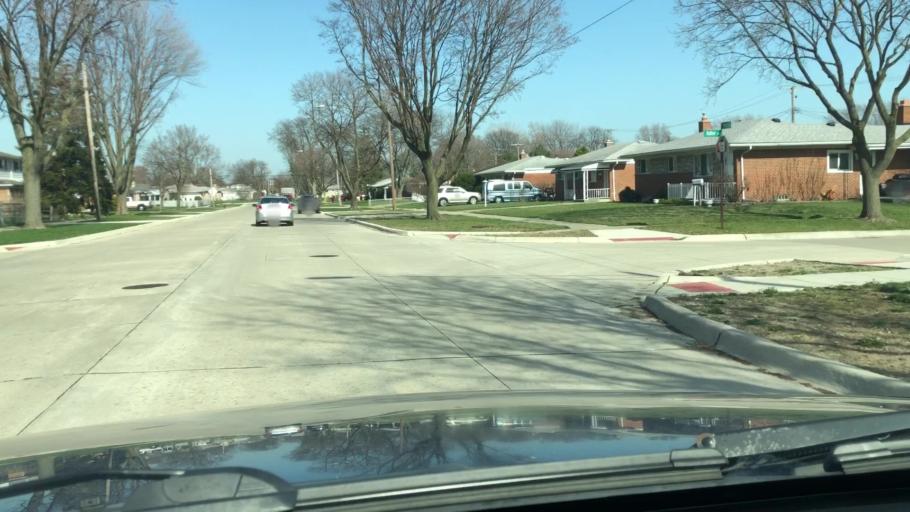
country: US
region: Michigan
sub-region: Macomb County
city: Center Line
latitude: 42.5001
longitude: -82.9942
